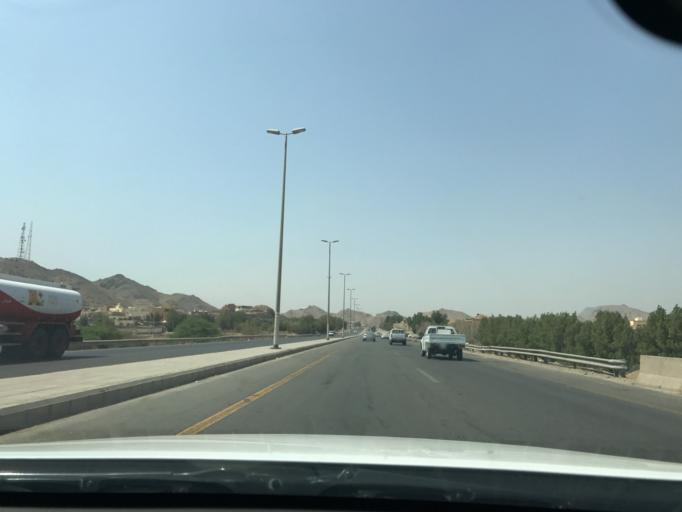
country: SA
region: Makkah
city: Jeddah
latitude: 21.3908
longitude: 39.4269
